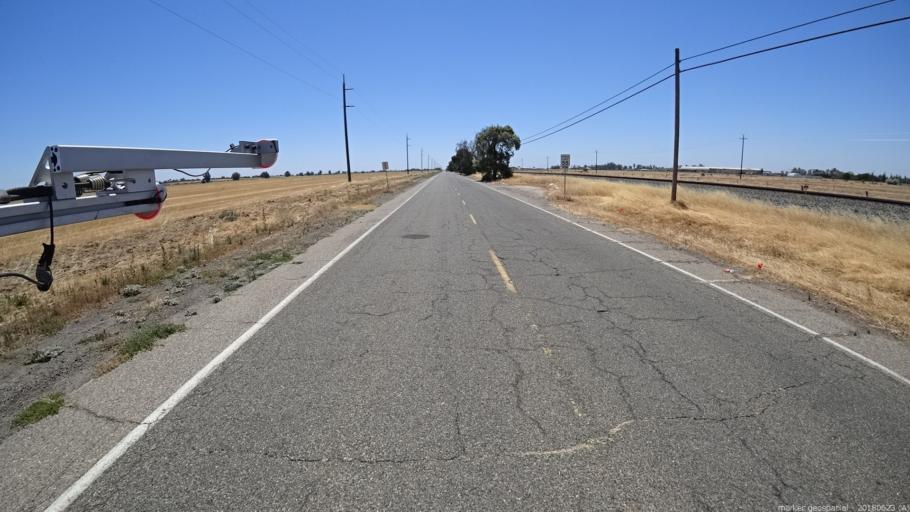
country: US
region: California
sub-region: Madera County
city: Chowchilla
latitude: 37.1167
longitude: -120.2468
